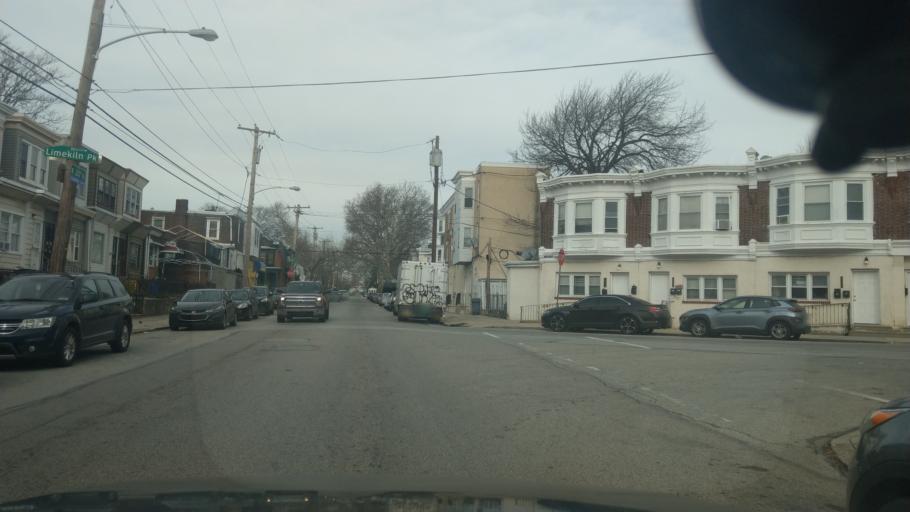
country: US
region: Pennsylvania
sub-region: Montgomery County
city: Wyncote
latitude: 40.0496
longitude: -75.1532
